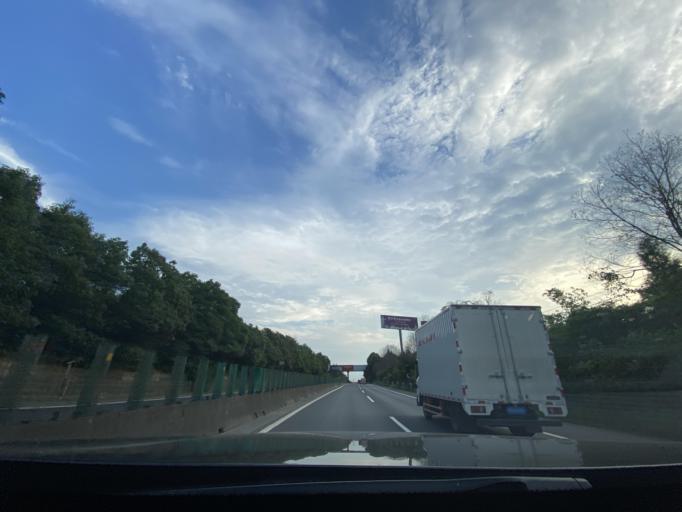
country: CN
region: Sichuan
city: Luojiang
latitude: 31.3951
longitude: 104.5621
